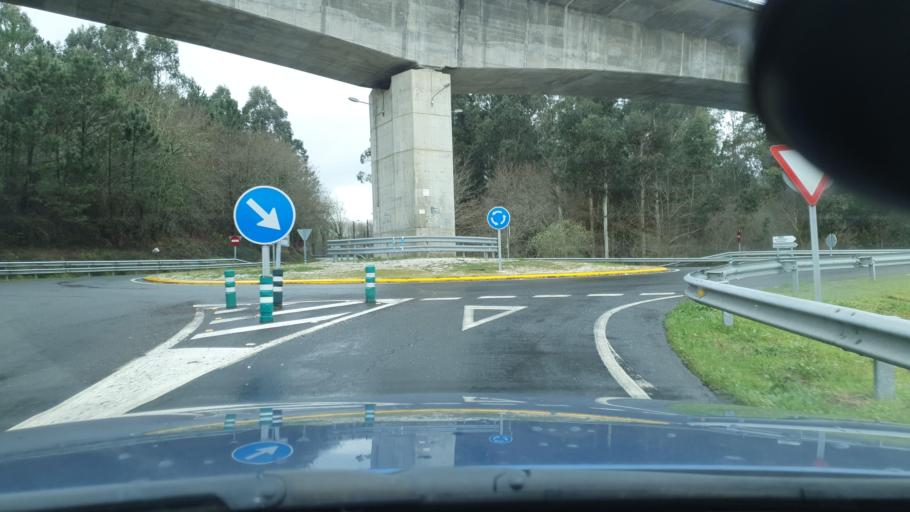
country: ES
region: Galicia
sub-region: Provincia da Coruna
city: Padron
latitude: 42.7550
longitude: -8.6776
